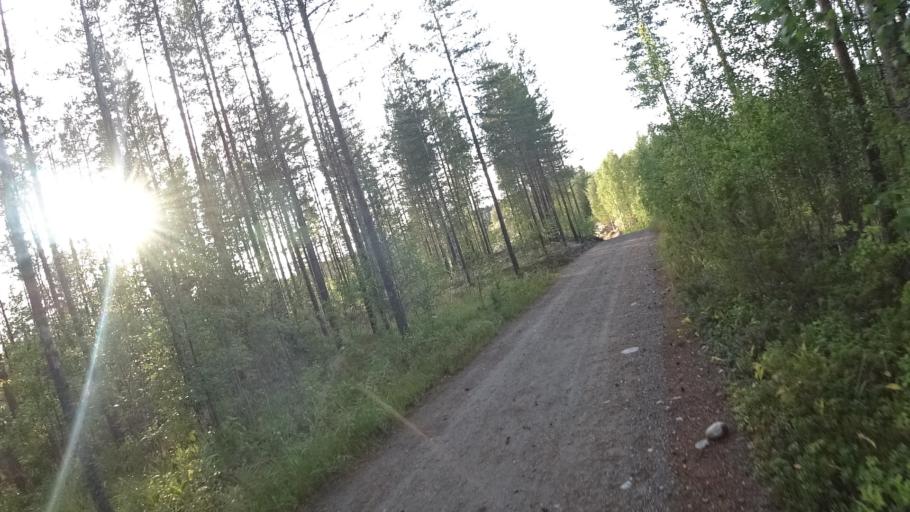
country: FI
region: North Karelia
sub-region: Joensuu
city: Ilomantsi
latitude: 62.6378
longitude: 31.0779
